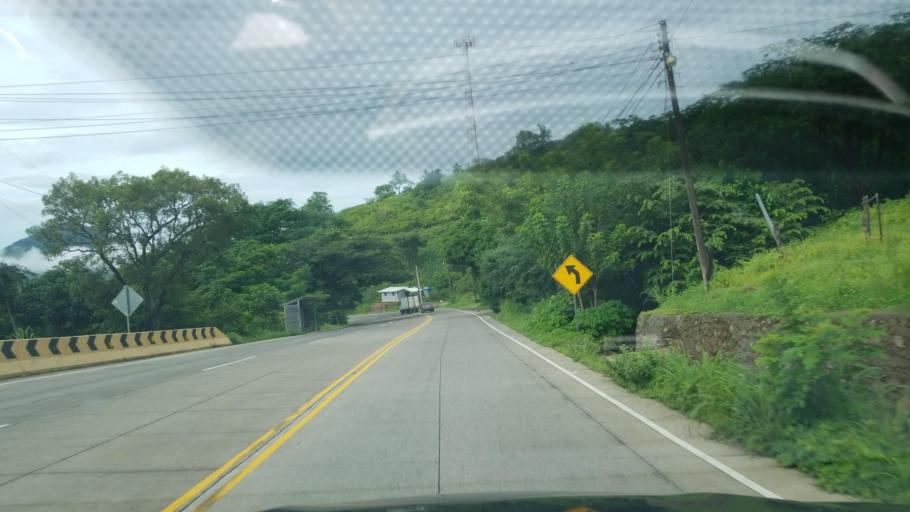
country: HN
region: Francisco Morazan
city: El Porvenir
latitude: 13.7031
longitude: -87.3157
